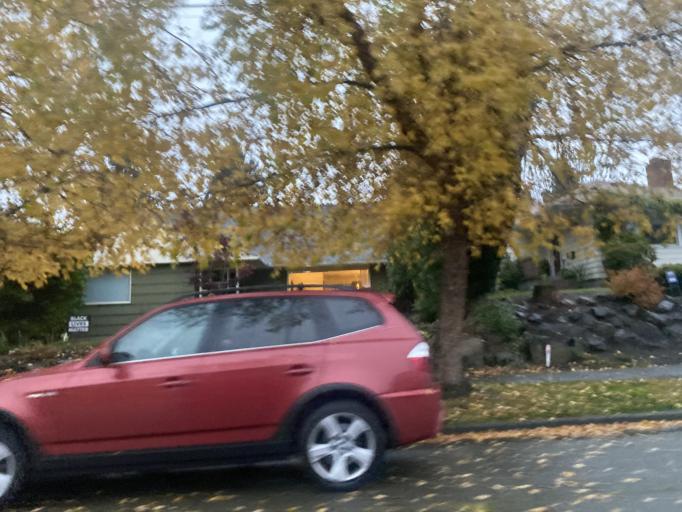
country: US
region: Washington
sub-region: King County
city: Seattle
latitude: 47.6496
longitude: -122.3929
